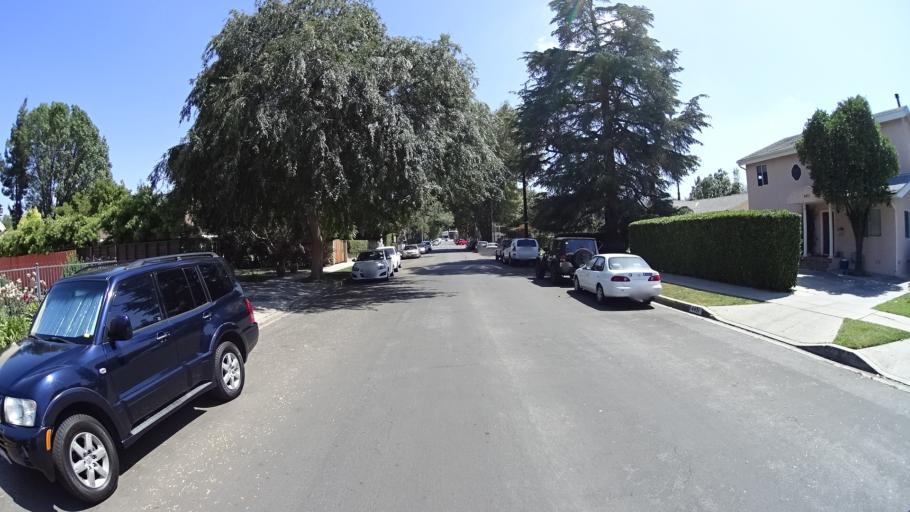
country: US
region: California
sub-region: Los Angeles County
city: Sherman Oaks
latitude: 34.1513
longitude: -118.4355
